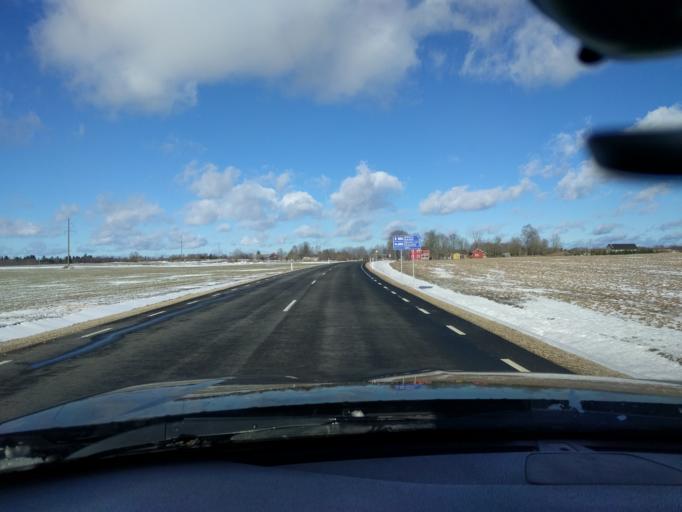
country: EE
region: Harju
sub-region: Raasiku vald
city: Raasiku
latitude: 59.2957
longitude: 25.1767
